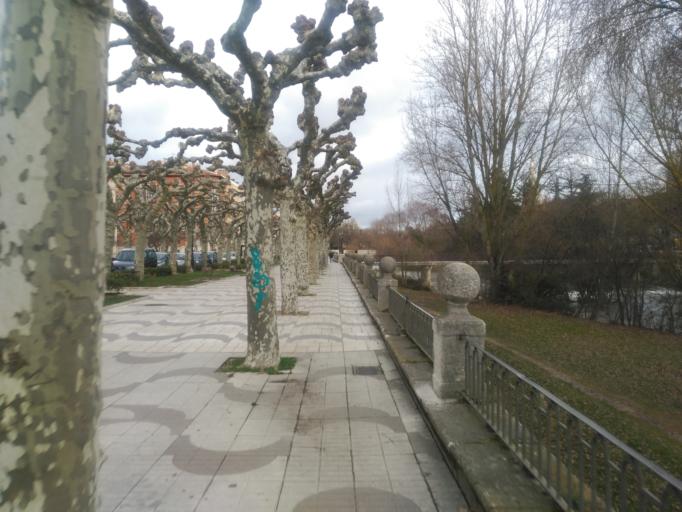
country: ES
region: Castille and Leon
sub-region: Provincia de Burgos
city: Burgos
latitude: 42.3377
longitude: -3.7067
